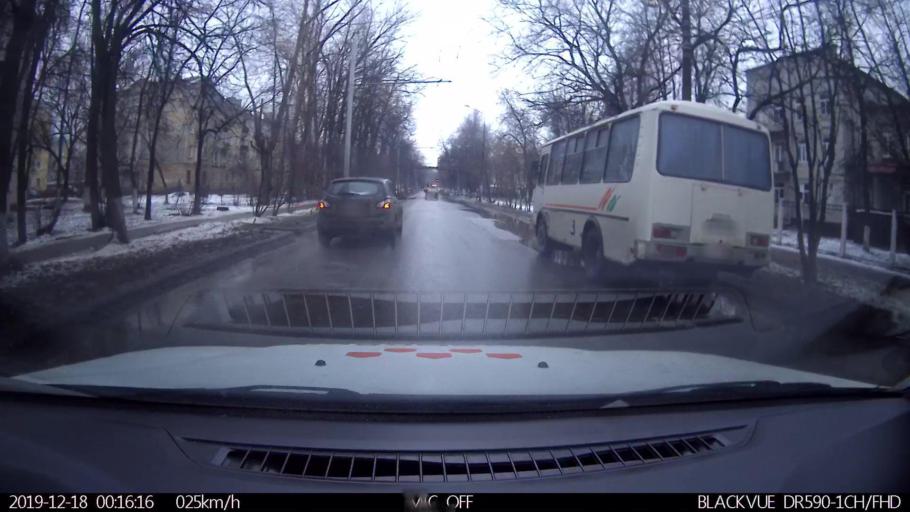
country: RU
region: Nizjnij Novgorod
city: Nizhniy Novgorod
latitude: 56.3291
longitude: 43.8788
